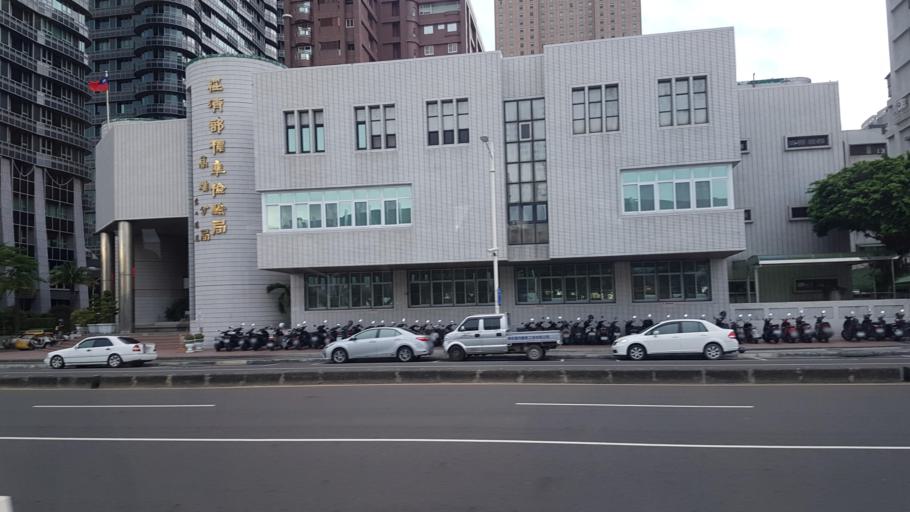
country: TW
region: Kaohsiung
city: Kaohsiung
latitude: 22.6183
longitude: 120.2934
